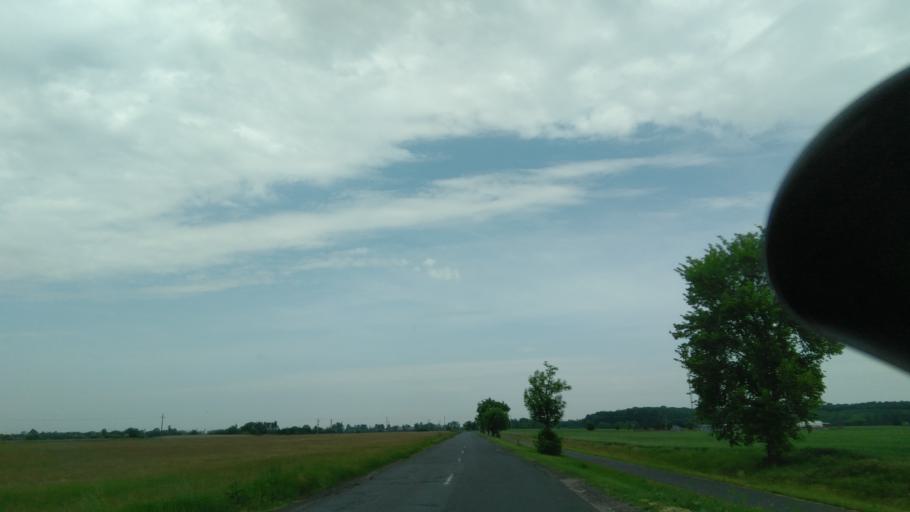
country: HU
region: Bekes
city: Fuzesgyarmat
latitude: 47.0703
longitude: 21.1966
